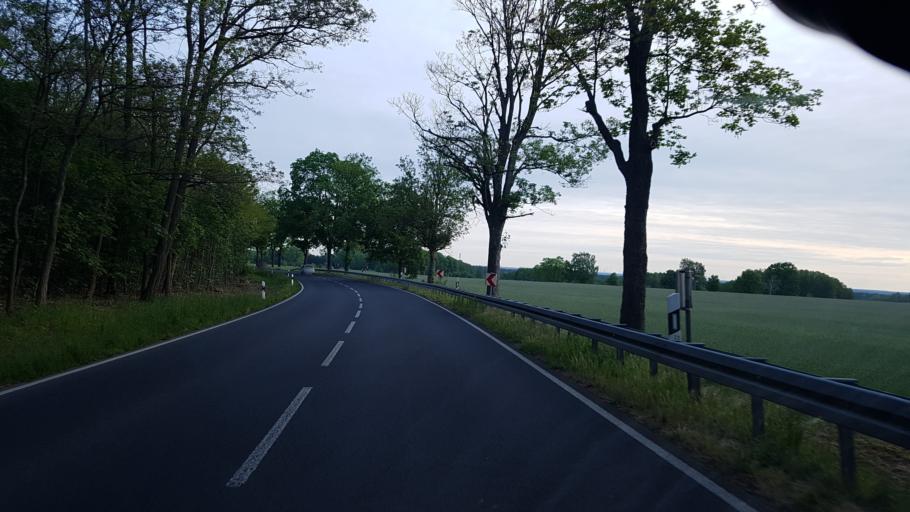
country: DE
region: Brandenburg
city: Sonnewalde
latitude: 51.7427
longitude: 13.6817
